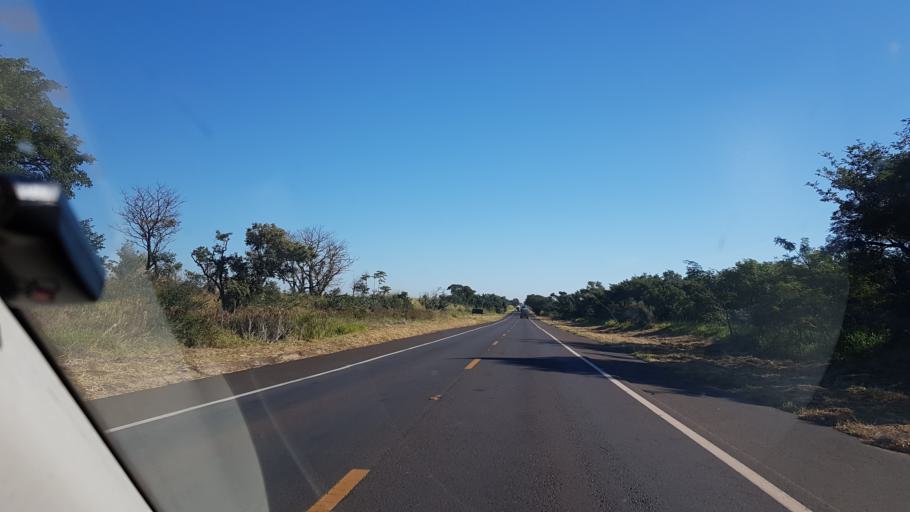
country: BR
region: Sao Paulo
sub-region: Maracai
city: Maracai
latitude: -22.5597
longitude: -50.5265
